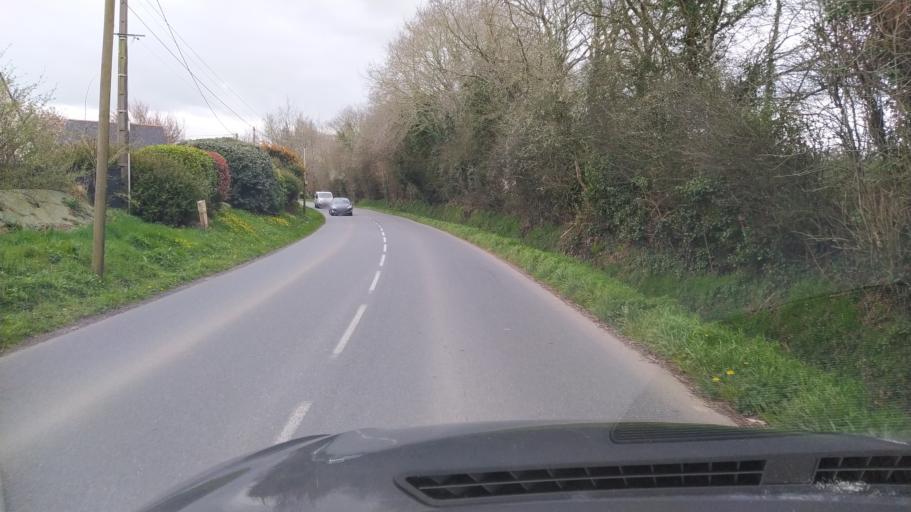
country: FR
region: Brittany
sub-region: Departement du Finistere
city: Bodilis
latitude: 48.5203
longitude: -4.1140
